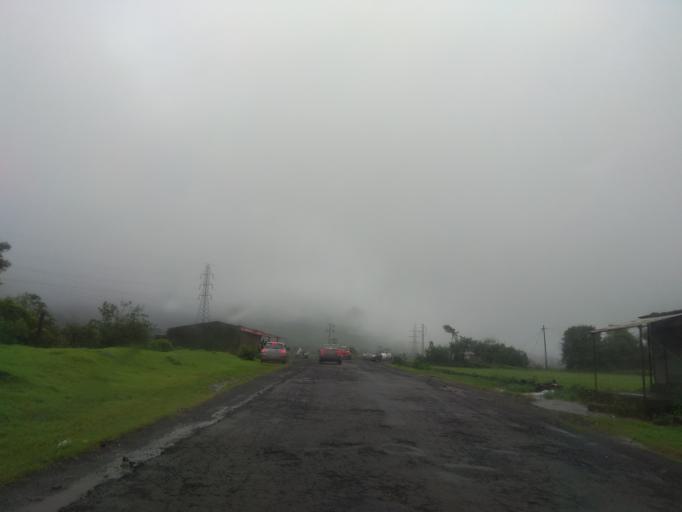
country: IN
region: Maharashtra
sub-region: Raigarh
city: Indapur
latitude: 18.4909
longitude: 73.4278
